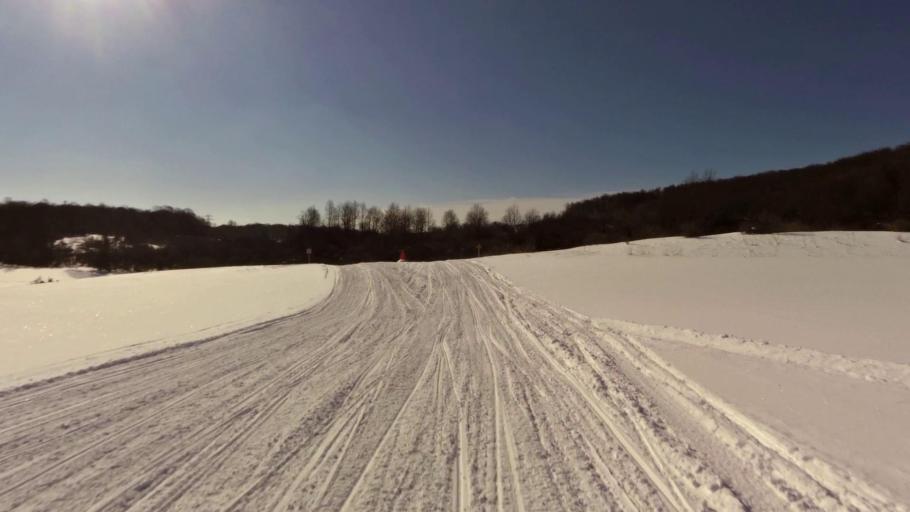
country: US
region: New York
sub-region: Cattaraugus County
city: Franklinville
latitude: 42.4017
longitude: -78.4987
